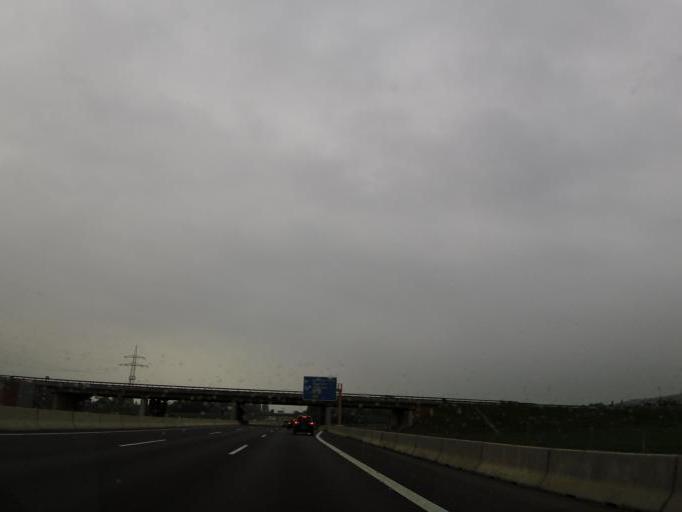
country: DE
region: Lower Saxony
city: Goettingen
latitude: 51.5579
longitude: 9.8790
